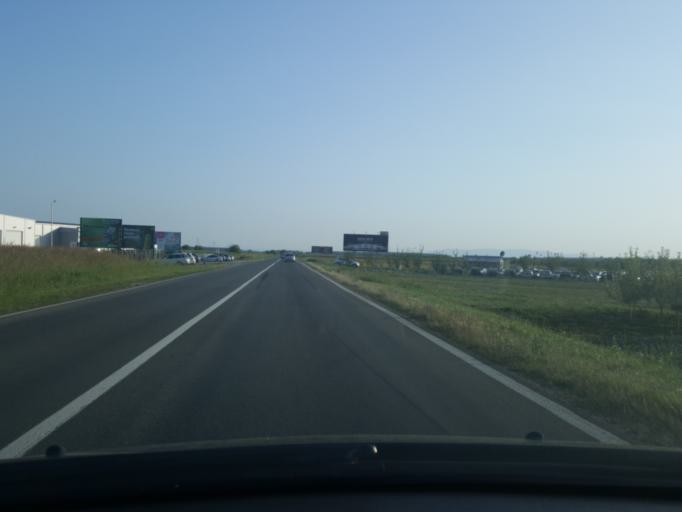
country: RS
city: Klenak
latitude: 44.7984
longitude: 19.7292
